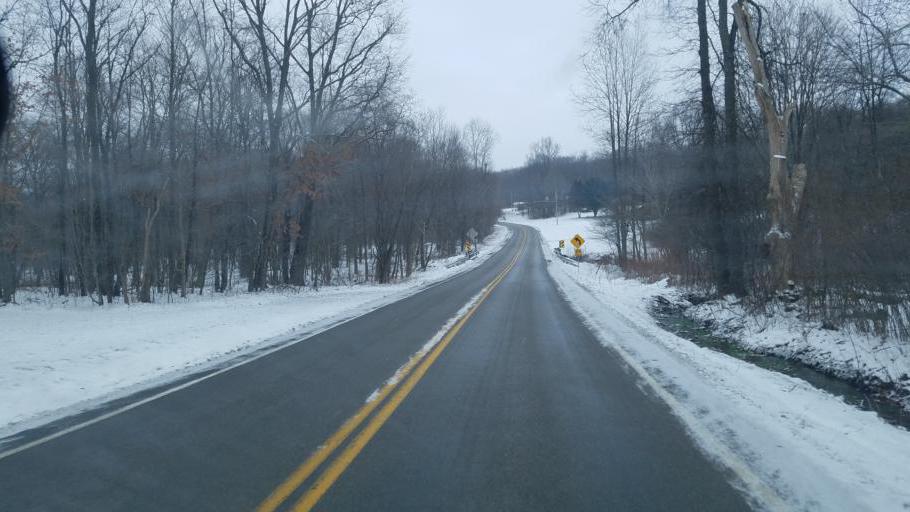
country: US
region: Pennsylvania
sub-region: Mercer County
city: Stoneboro
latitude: 41.4111
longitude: -80.0731
